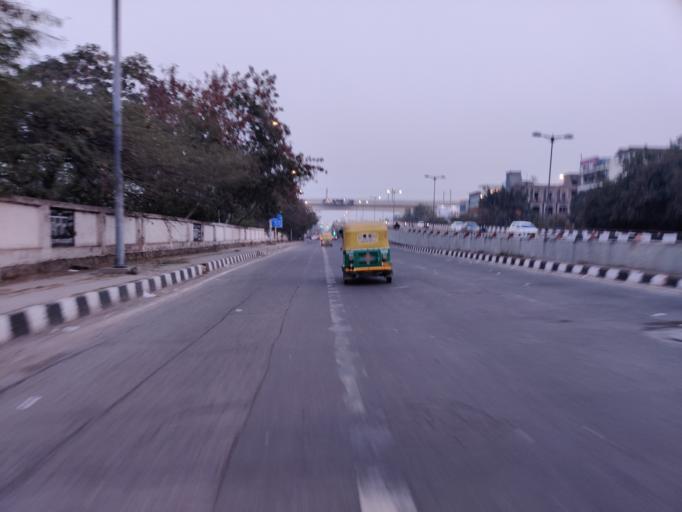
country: IN
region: NCT
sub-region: North Delhi
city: Delhi
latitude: 28.6461
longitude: 77.2972
